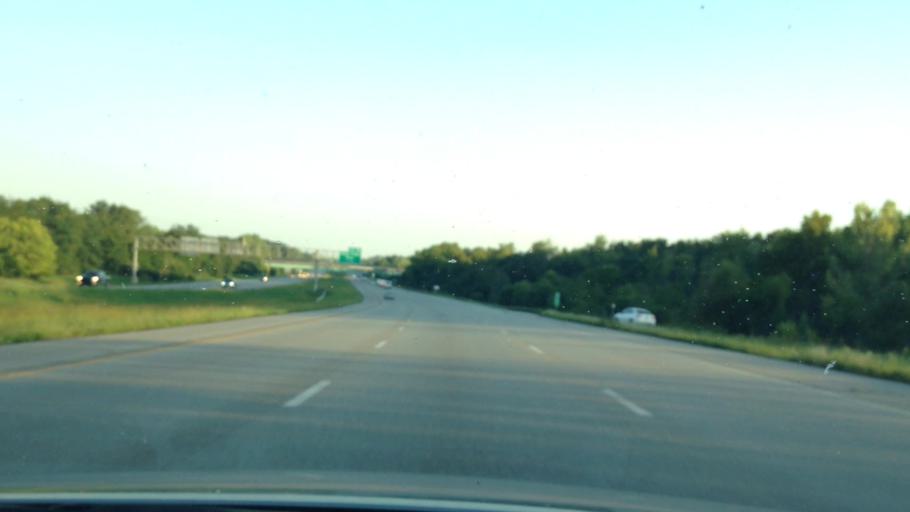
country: US
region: Missouri
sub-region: Clay County
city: Pleasant Valley
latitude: 39.2390
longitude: -94.5069
